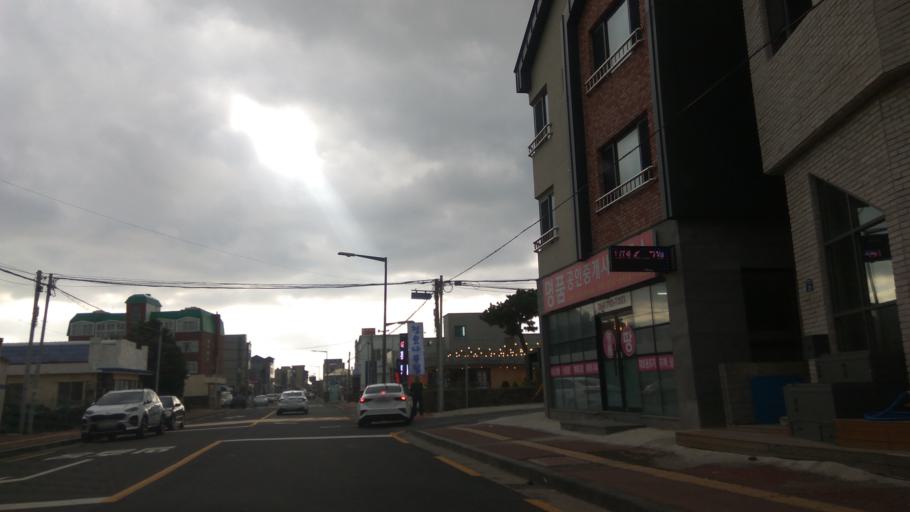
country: KR
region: Jeju-do
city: Jeju-si
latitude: 33.4625
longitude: 126.9328
